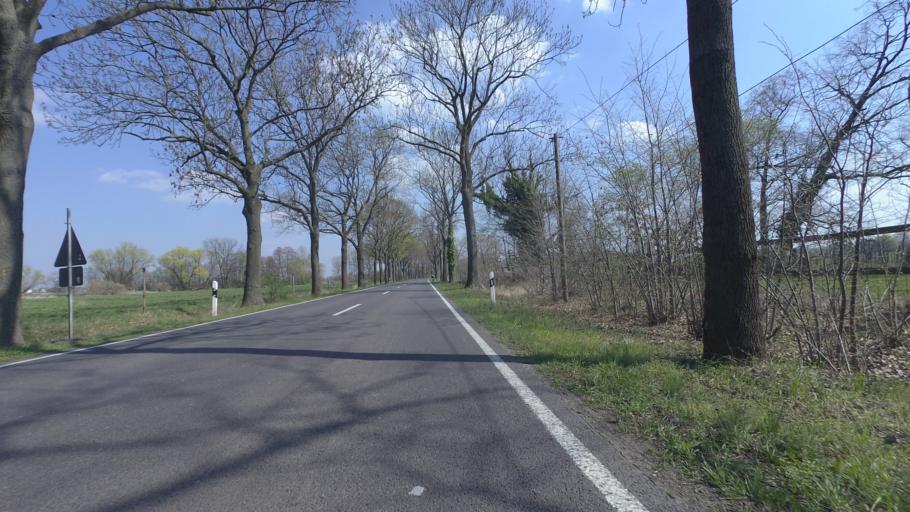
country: DE
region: Brandenburg
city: Mittenwalde
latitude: 52.2715
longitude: 13.5185
